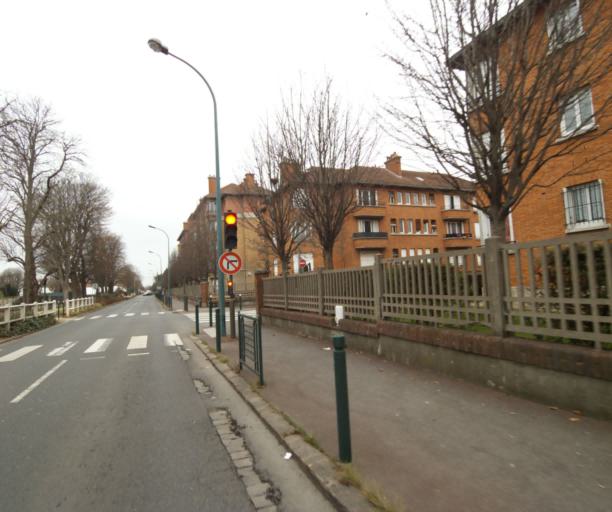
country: FR
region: Ile-de-France
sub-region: Departement des Hauts-de-Seine
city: Saint-Cloud
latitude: 48.8610
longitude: 2.2017
